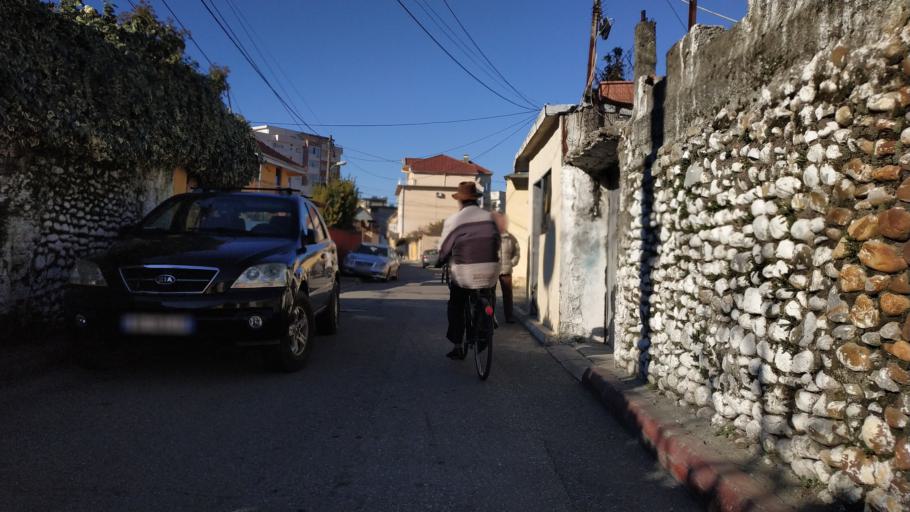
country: AL
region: Shkoder
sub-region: Rrethi i Shkodres
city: Shkoder
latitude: 42.0730
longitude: 19.5181
